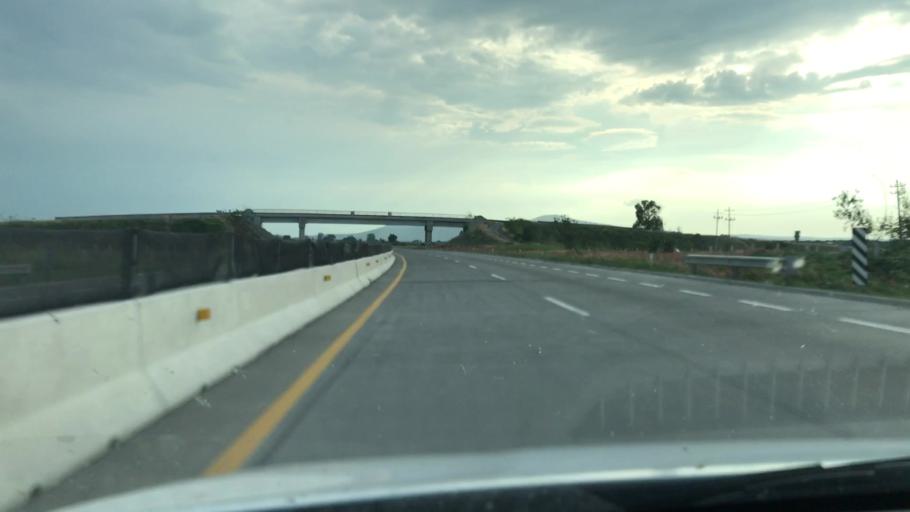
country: MX
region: Michoacan
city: La Piedad Cavadas
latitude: 20.3906
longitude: -102.1027
